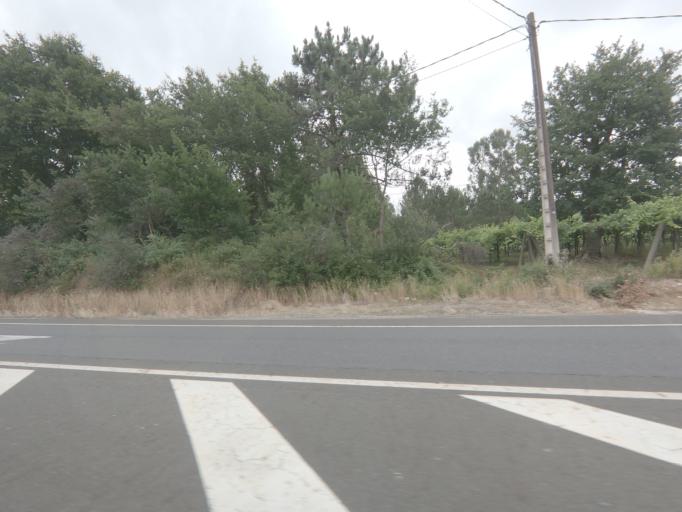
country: ES
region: Galicia
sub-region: Provincia de Pontevedra
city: Tomino
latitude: 41.9705
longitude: -8.7570
